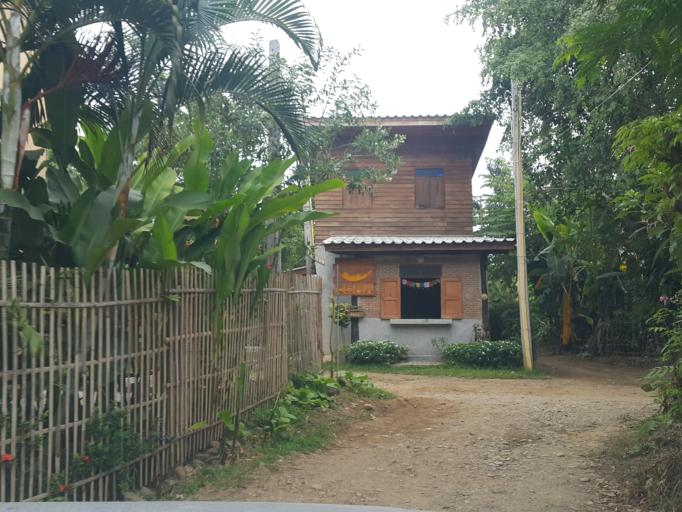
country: TH
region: Chiang Mai
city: Pai
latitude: 19.3600
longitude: 98.4454
